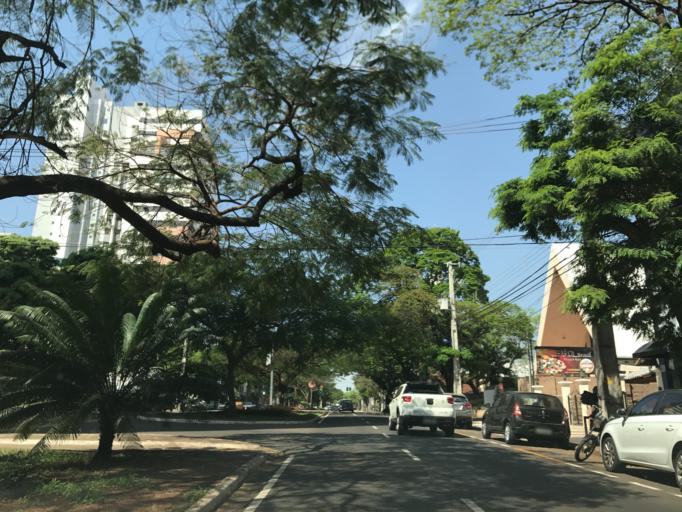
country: BR
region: Parana
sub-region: Maringa
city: Maringa
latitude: -23.4258
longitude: -51.9422
